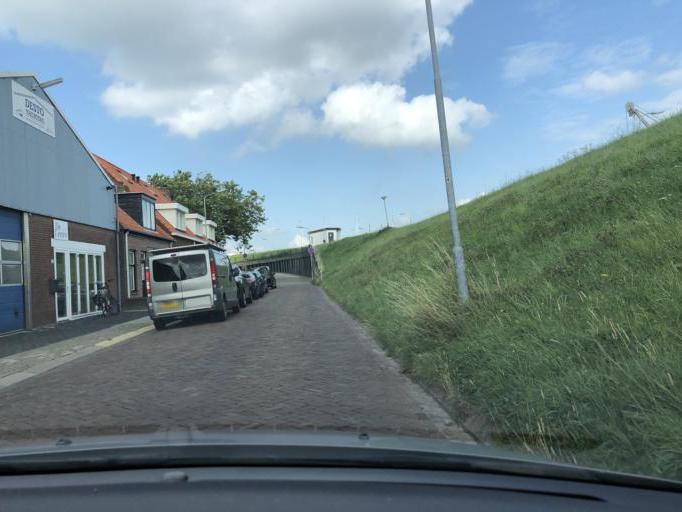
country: NL
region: Zeeland
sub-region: Gemeente Reimerswaal
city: Yerseke
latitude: 51.4967
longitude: 4.0526
